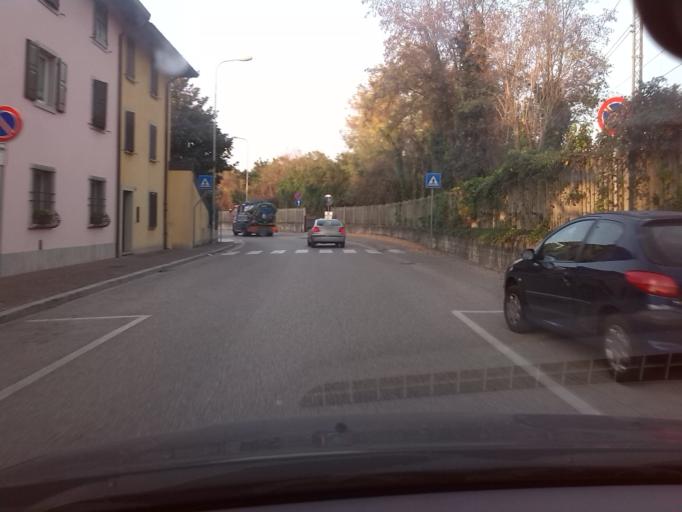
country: IT
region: Friuli Venezia Giulia
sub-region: Provincia di Udine
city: Udine
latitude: 46.0514
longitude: 13.2301
